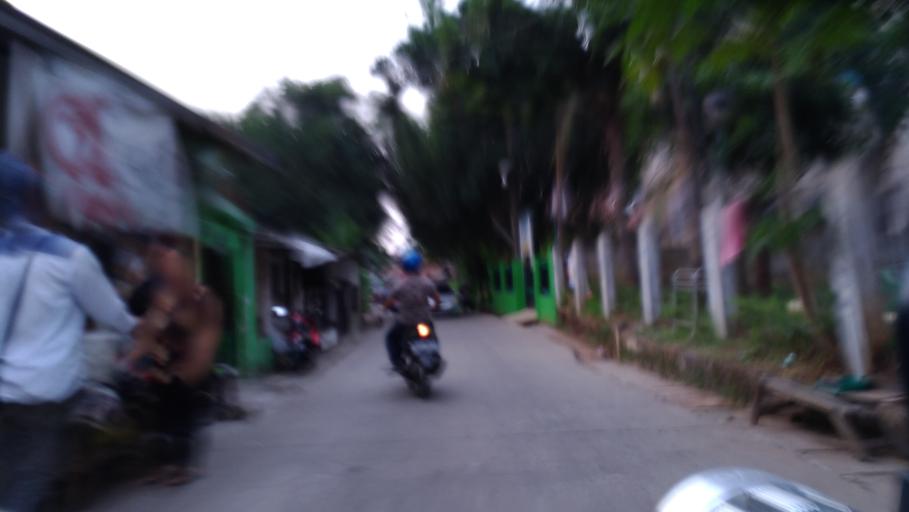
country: ID
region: West Java
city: Depok
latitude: -6.3584
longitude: 106.8705
